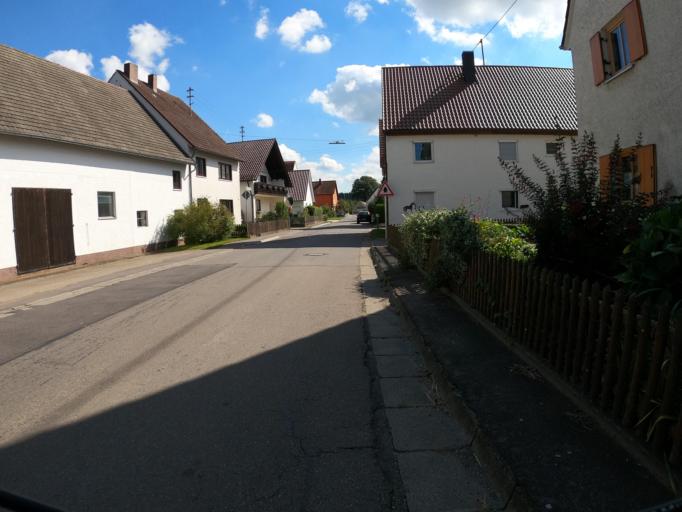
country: DE
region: Bavaria
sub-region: Swabia
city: Pfaffenhofen an der Roth
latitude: 48.3327
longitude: 10.2062
